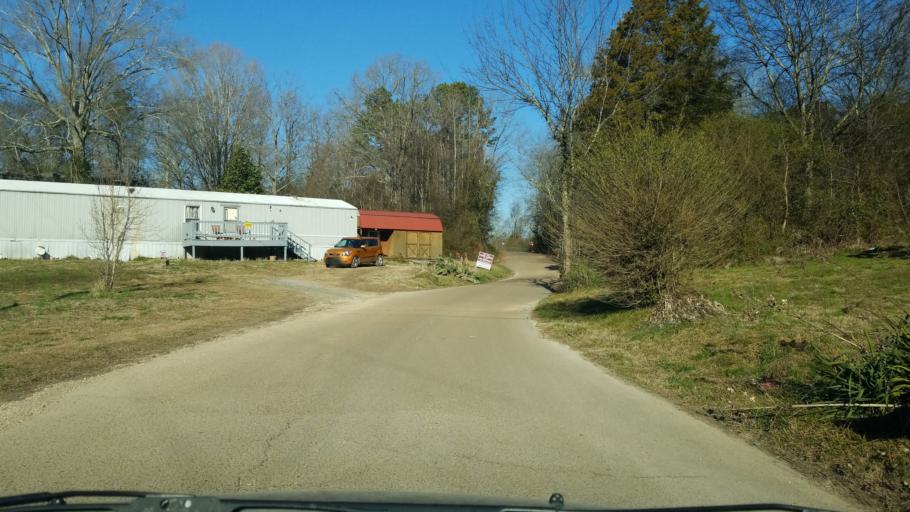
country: US
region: Tennessee
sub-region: Hamilton County
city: Collegedale
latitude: 35.0708
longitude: -85.1007
